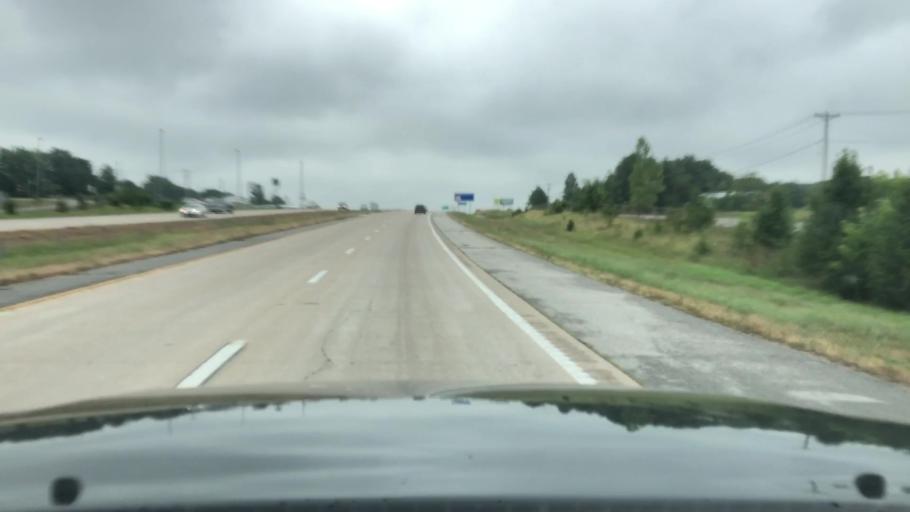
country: US
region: Missouri
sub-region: Saint Charles County
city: Wentzville
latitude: 38.8017
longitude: -90.8285
